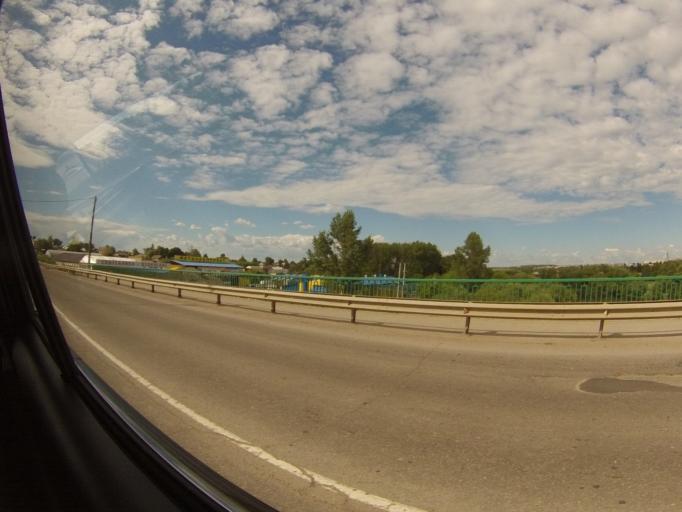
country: RU
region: Orjol
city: Mtsensk
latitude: 53.2833
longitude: 36.5653
